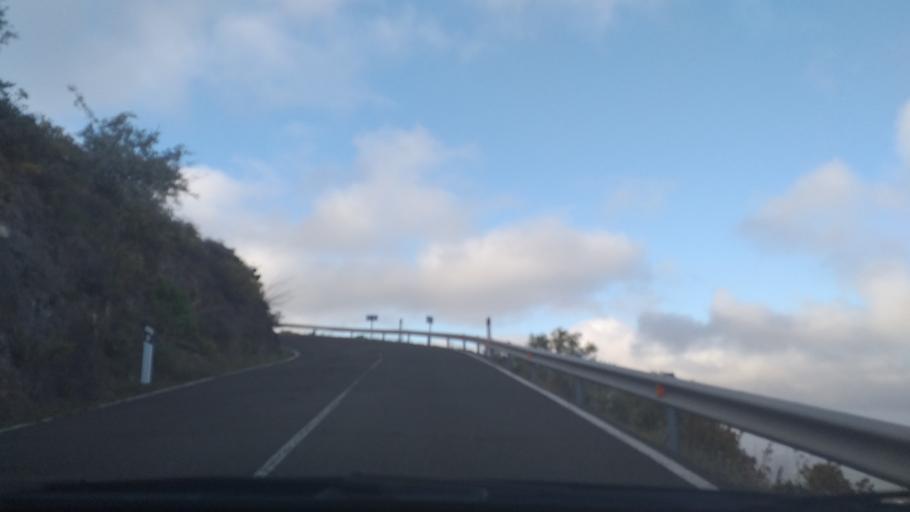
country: ES
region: Canary Islands
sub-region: Provincia de Las Palmas
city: Valsequillo de Gran Canaria
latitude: 27.9569
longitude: -15.4951
